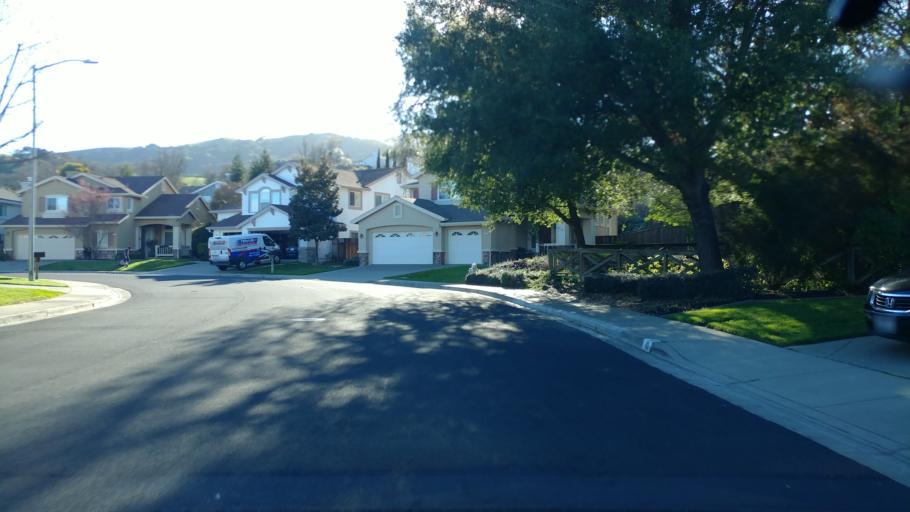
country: US
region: California
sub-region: Contra Costa County
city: San Ramon
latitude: 37.7455
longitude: -121.9596
